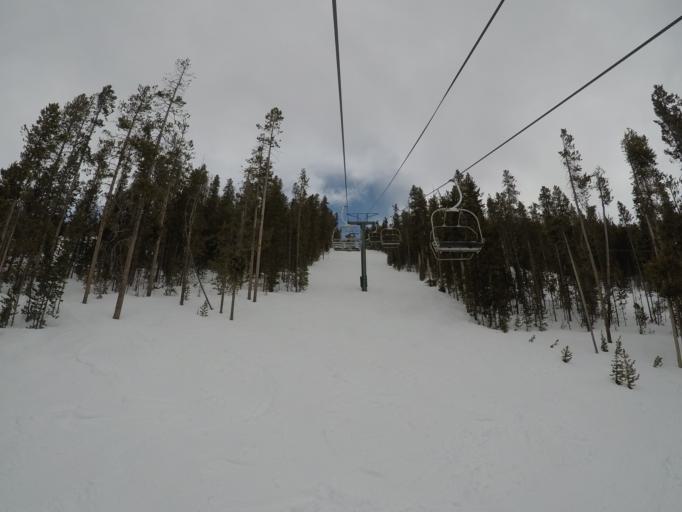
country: US
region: Montana
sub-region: Granite County
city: Philipsburg
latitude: 46.2573
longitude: -113.2446
